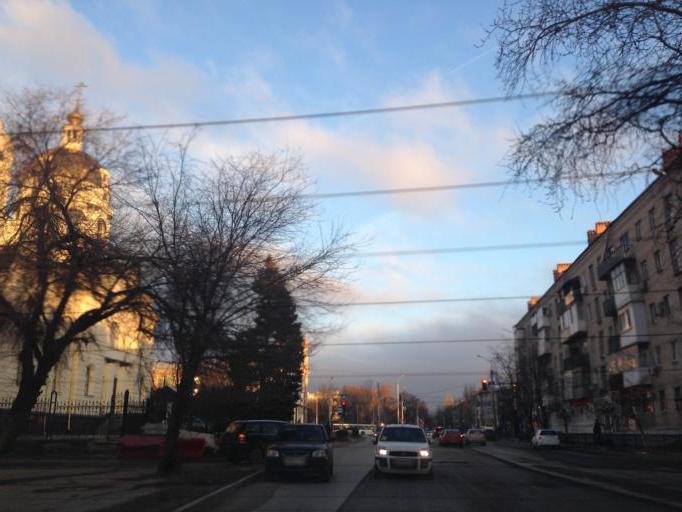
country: RU
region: Rostov
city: Rostov-na-Donu
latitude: 47.2501
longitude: 39.6952
